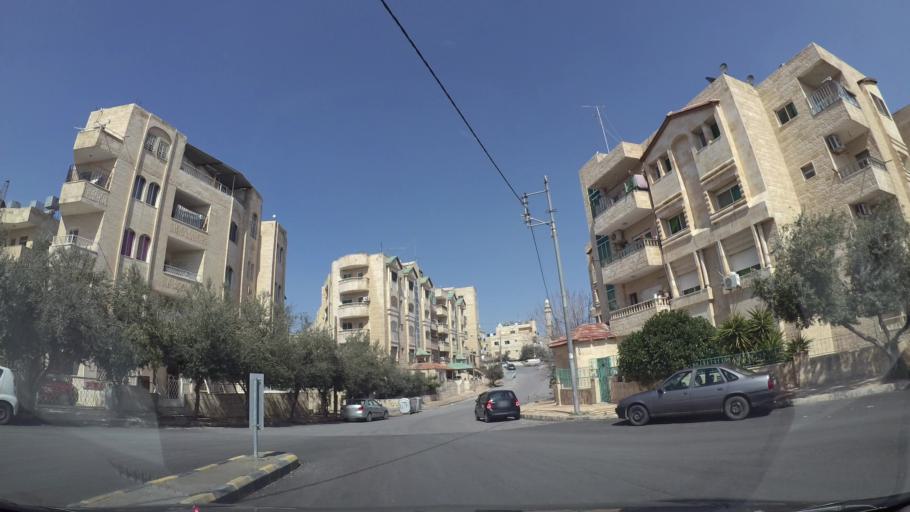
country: JO
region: Amman
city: Amman
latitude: 31.9749
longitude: 35.9908
